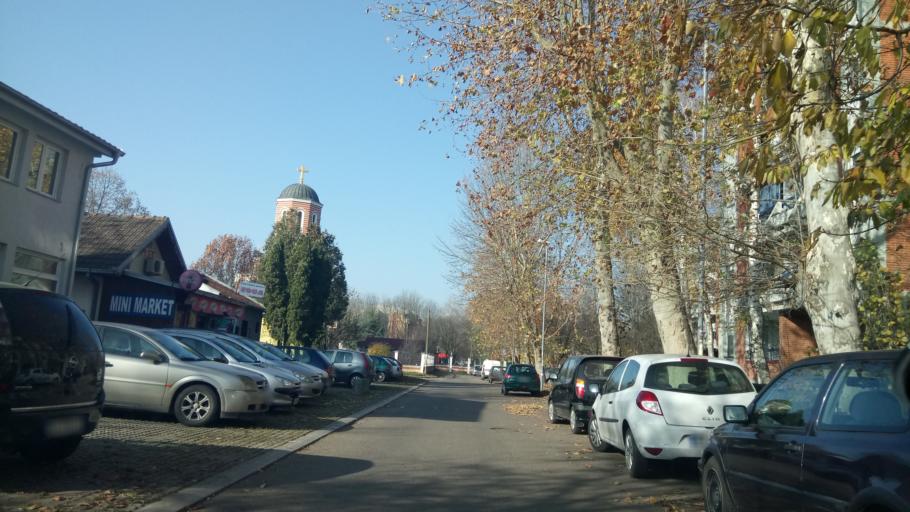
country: RS
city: Novi Banovci
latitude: 44.8938
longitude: 20.2935
